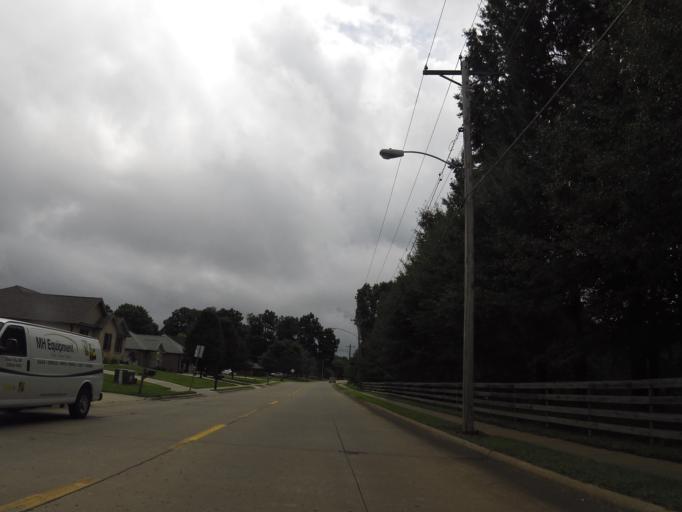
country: US
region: Missouri
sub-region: Cape Girardeau County
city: Cape Girardeau
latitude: 37.3421
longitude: -89.5557
